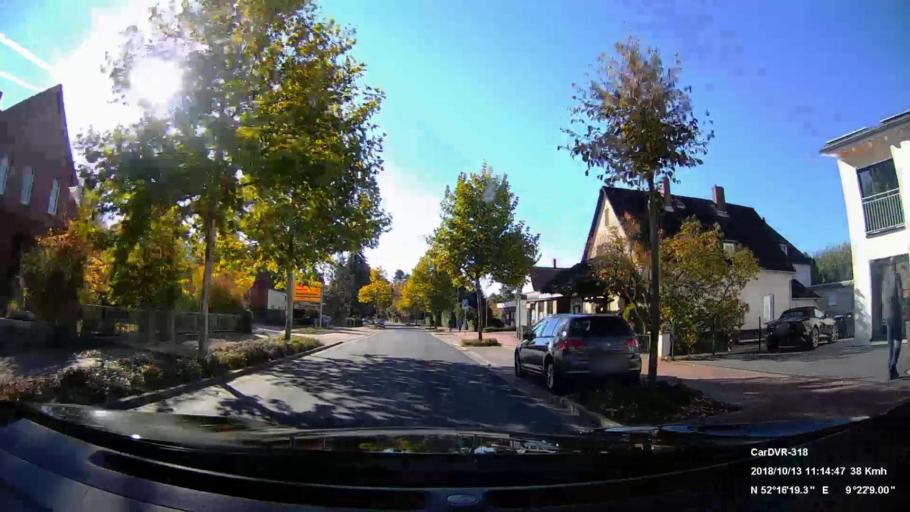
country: DE
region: Lower Saxony
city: Lauenau
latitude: 52.2720
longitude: 9.3692
